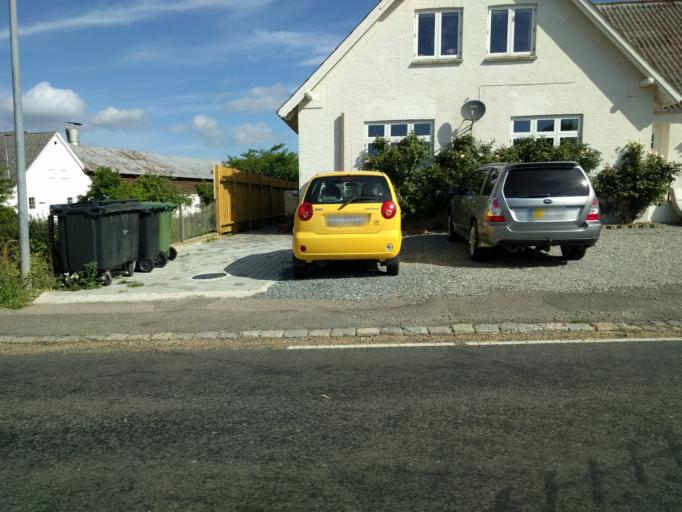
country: DK
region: Zealand
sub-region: Vordingborg Kommune
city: Stege
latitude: 54.9594
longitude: 12.2453
